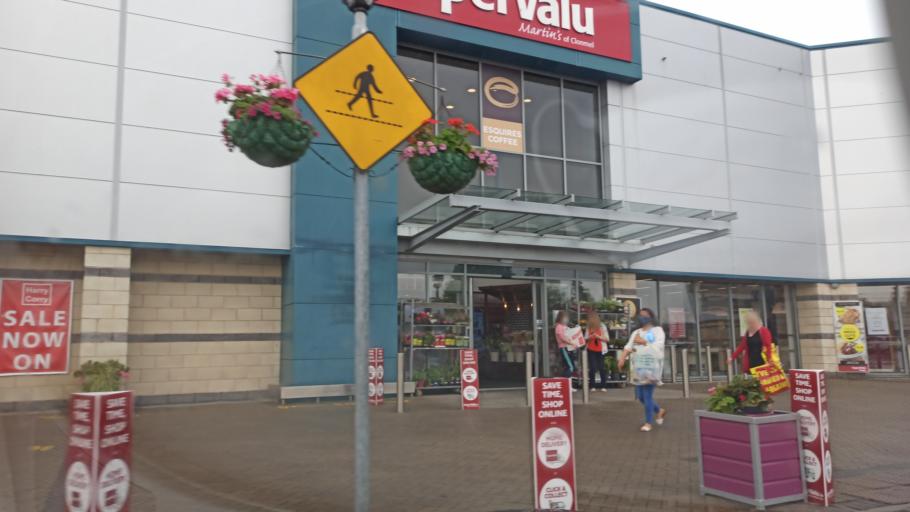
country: IE
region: Munster
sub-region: South Tipperary
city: Cluain Meala
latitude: 52.3566
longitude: -7.7361
